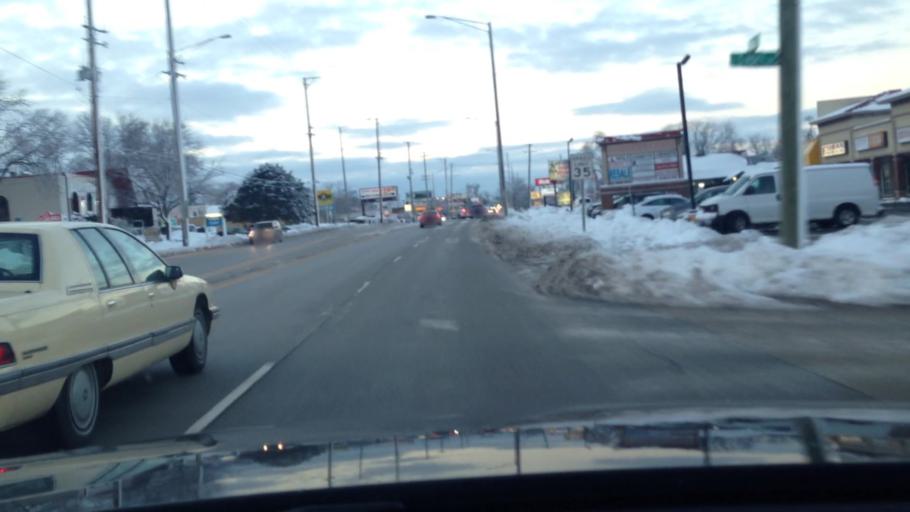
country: US
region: Illinois
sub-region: Cook County
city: Palatine
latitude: 42.1398
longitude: -88.0227
